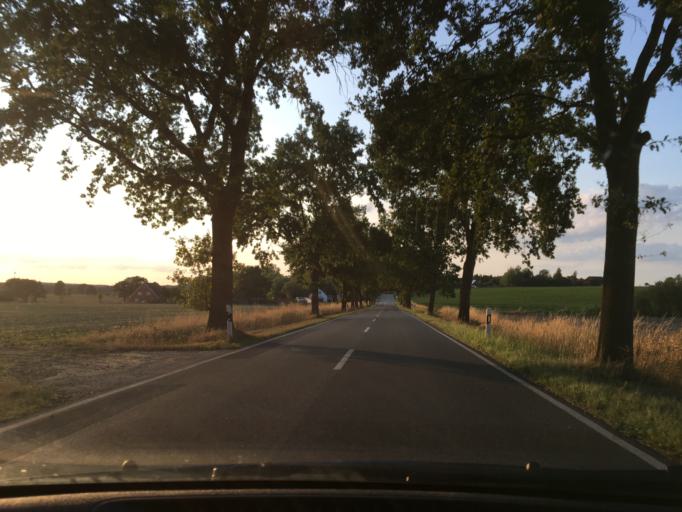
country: DE
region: Lower Saxony
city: Bleckede
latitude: 53.2503
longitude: 10.7696
